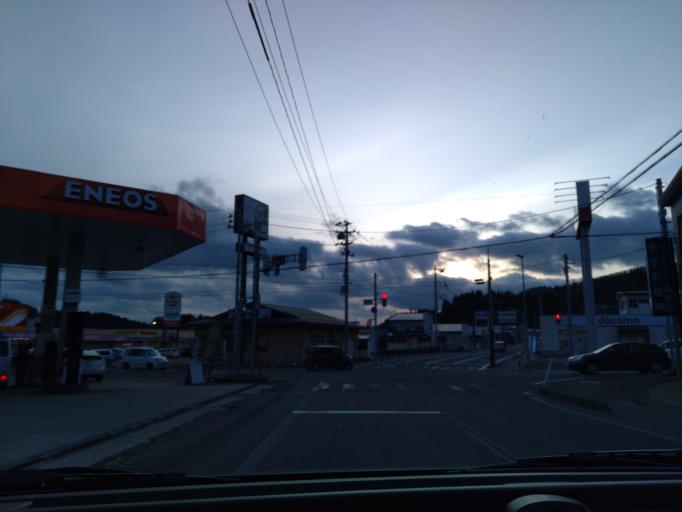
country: JP
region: Akita
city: Kakunodatemachi
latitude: 39.5941
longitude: 140.5771
